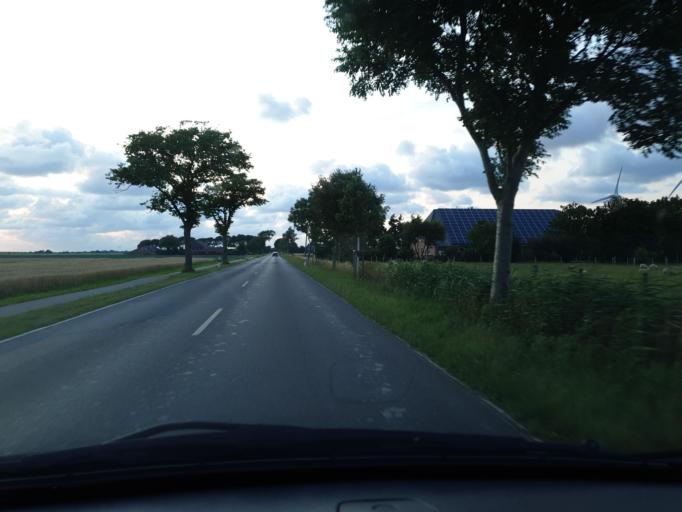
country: DE
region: Schleswig-Holstein
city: Friedrichskoog
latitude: 53.9765
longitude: 8.9209
